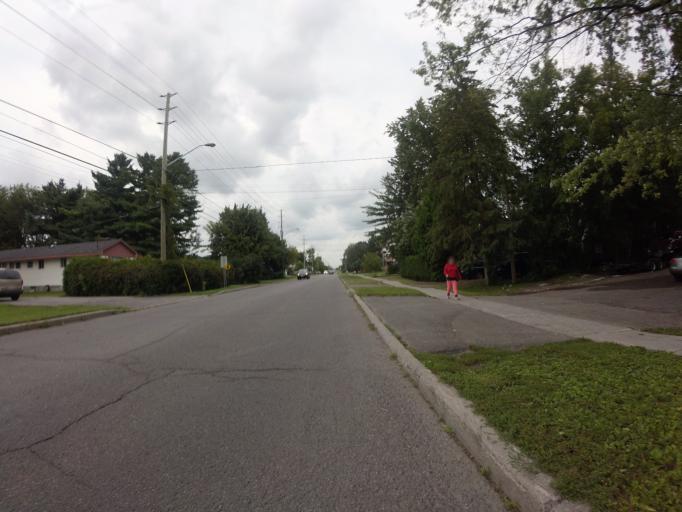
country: CA
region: Quebec
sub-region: Outaouais
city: Gatineau
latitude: 45.4550
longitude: -75.5125
